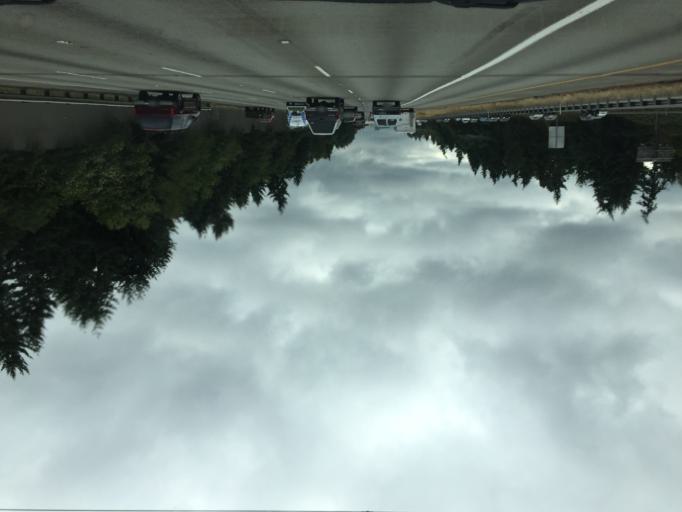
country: US
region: Washington
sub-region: King County
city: Lakeland North
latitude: 47.3433
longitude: -122.2930
